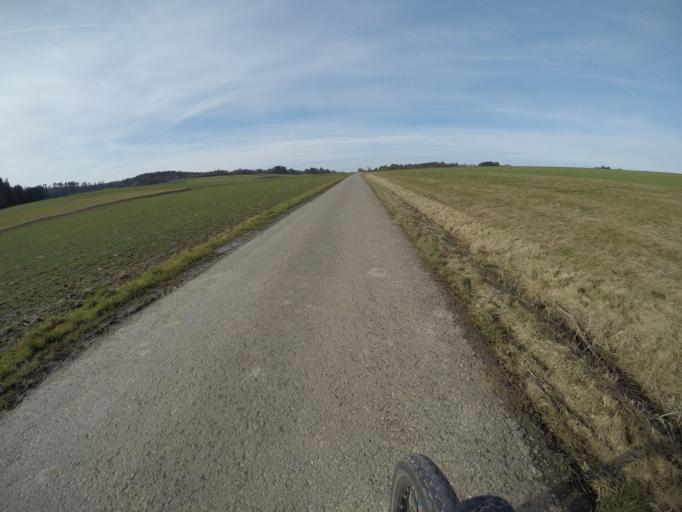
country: DE
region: Baden-Wuerttemberg
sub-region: Karlsruhe Region
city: Althengstett
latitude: 48.6940
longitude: 8.7948
